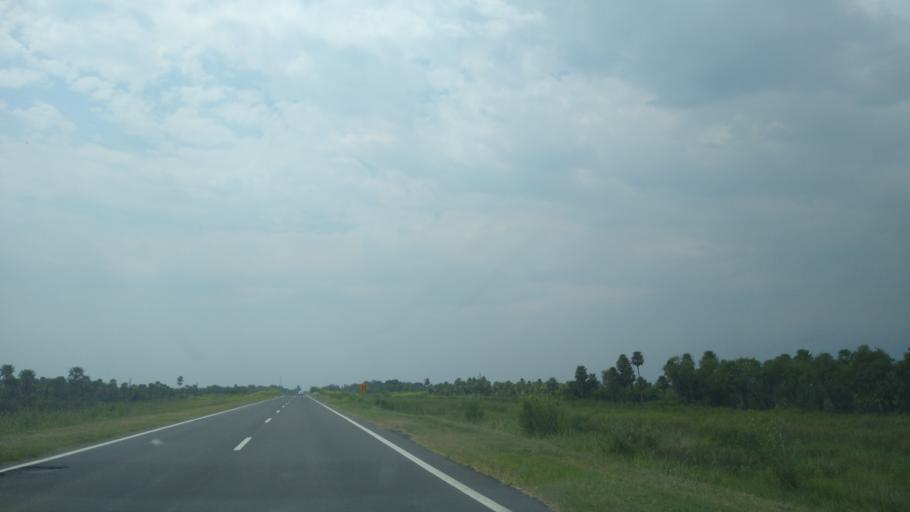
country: AR
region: Chaco
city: Margarita Belen
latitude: -27.1125
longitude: -58.9683
